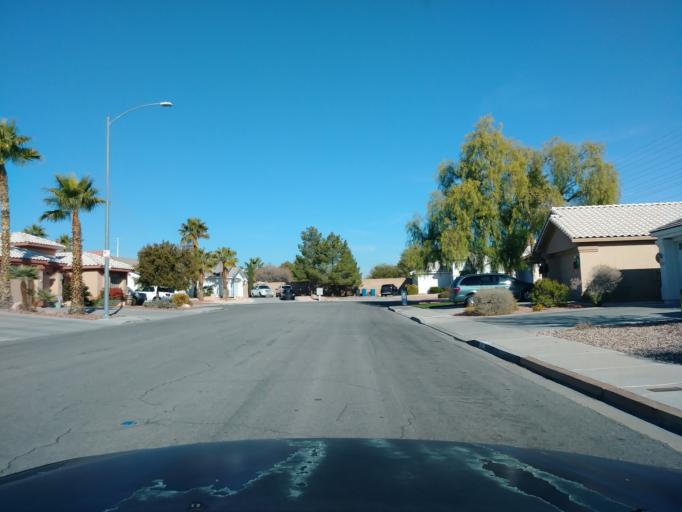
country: US
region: Nevada
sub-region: Clark County
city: Spring Valley
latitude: 36.1489
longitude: -115.2777
